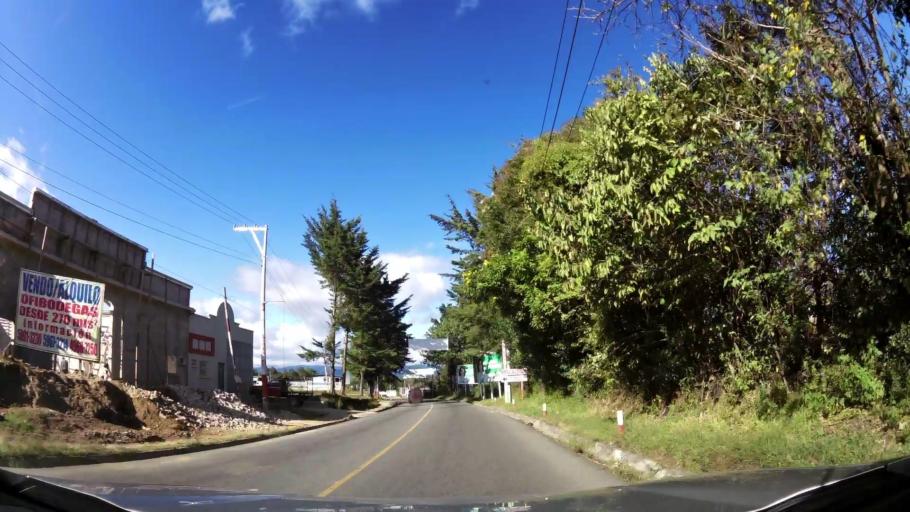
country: GT
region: Quiche
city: Chichicastenango
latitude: 14.9556
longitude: -91.1062
